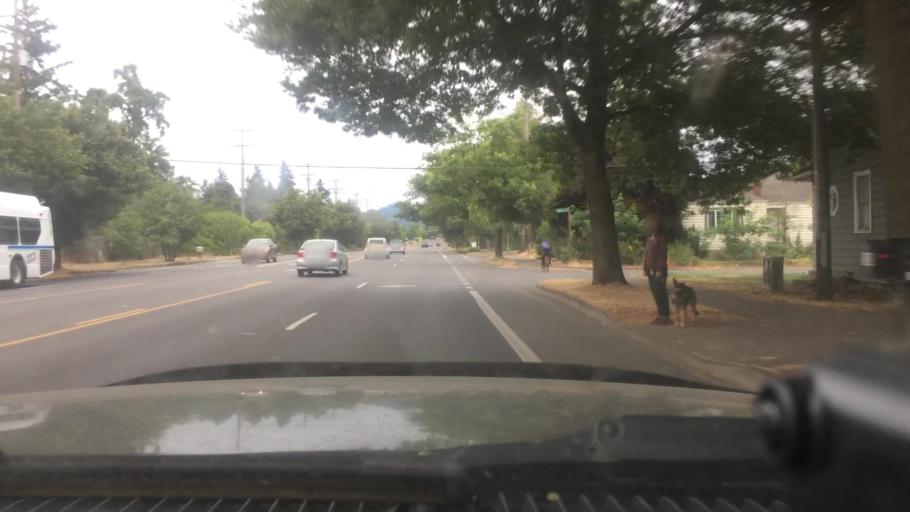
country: US
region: Oregon
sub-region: Lane County
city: Eugene
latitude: 44.0691
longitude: -123.1182
